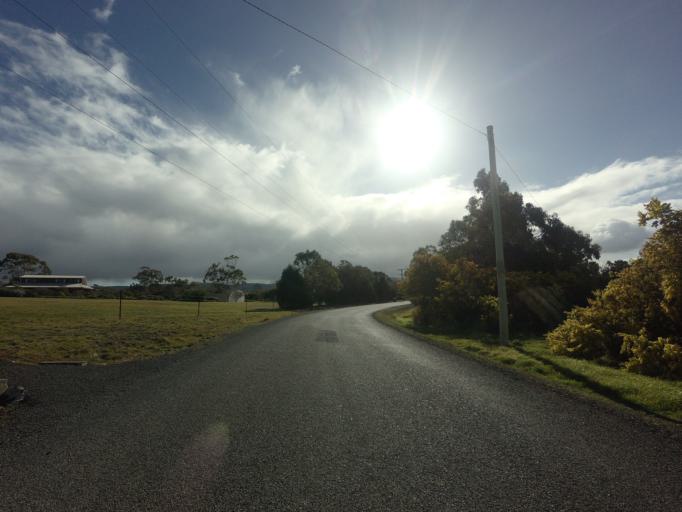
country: AU
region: Tasmania
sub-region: Sorell
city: Sorell
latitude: -42.3072
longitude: 147.9909
